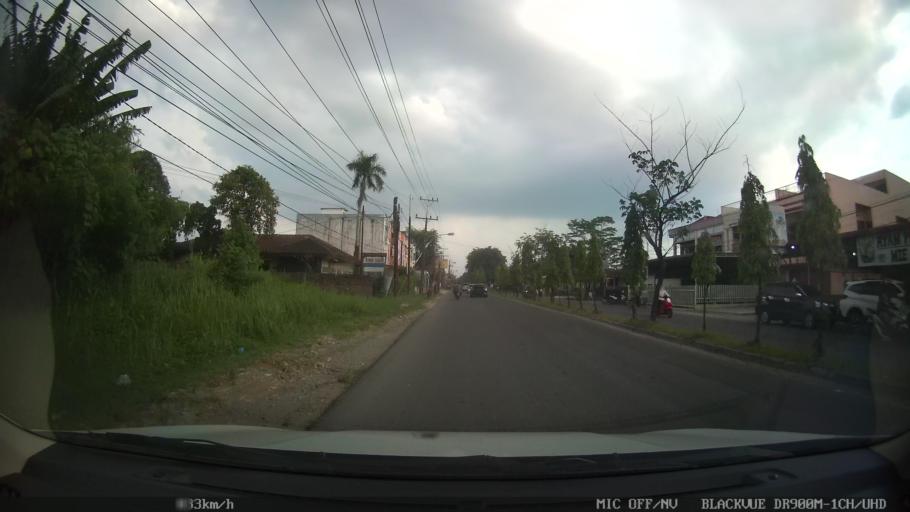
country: ID
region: North Sumatra
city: Sunggal
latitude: 3.5380
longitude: 98.6224
